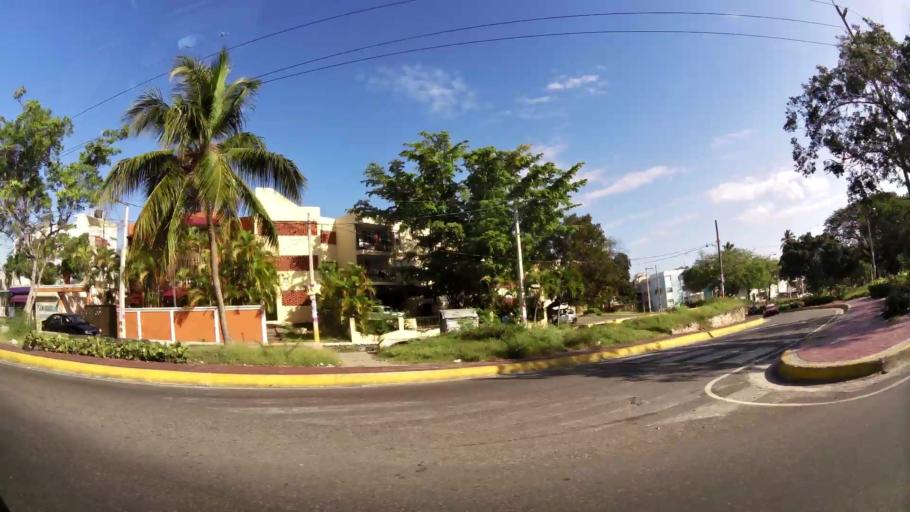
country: DO
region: Nacional
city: San Carlos
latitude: 18.4818
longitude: -69.8792
